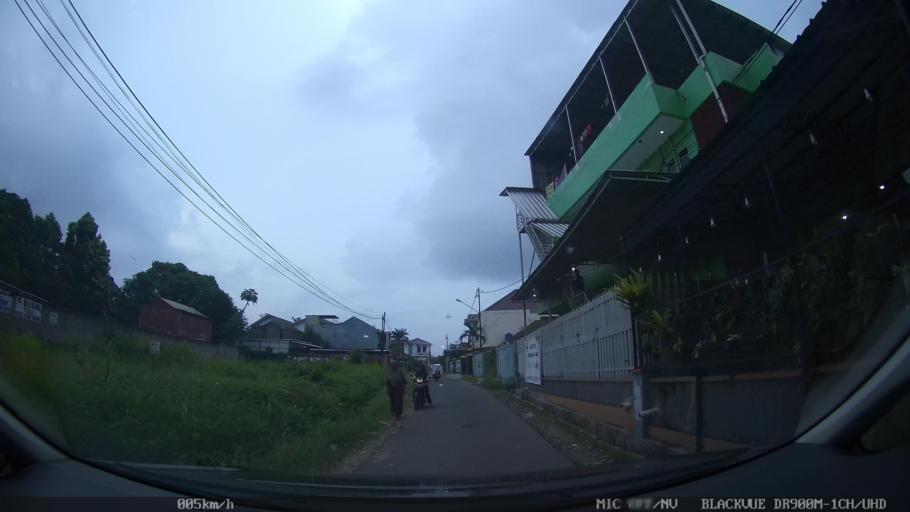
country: ID
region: Lampung
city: Bandarlampung
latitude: -5.4124
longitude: 105.2747
